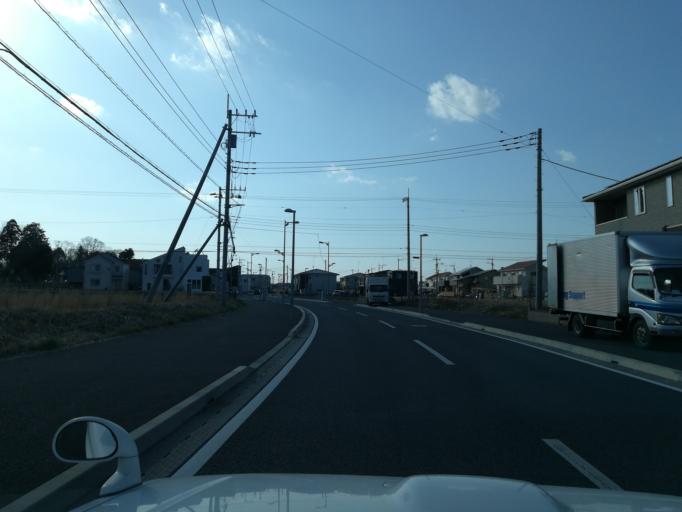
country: JP
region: Ibaraki
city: Naka
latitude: 36.0969
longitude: 140.0868
